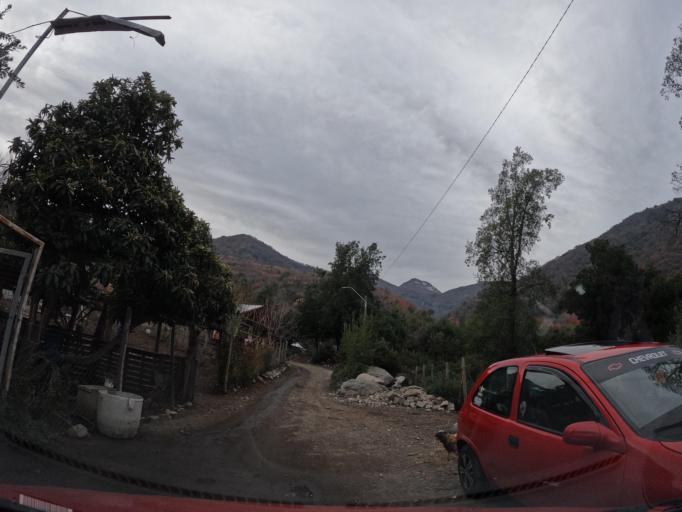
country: CL
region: Maule
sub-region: Provincia de Linares
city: Colbun
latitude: -35.7237
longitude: -71.0177
